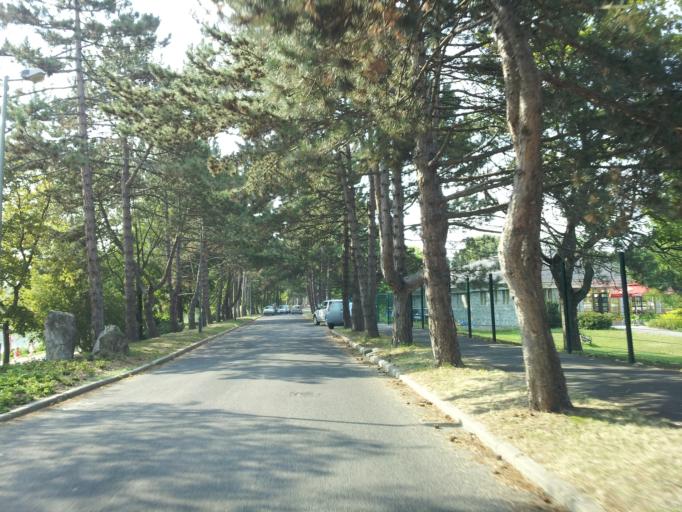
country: HU
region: Vas
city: Szombathely
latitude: 47.2346
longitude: 16.6026
